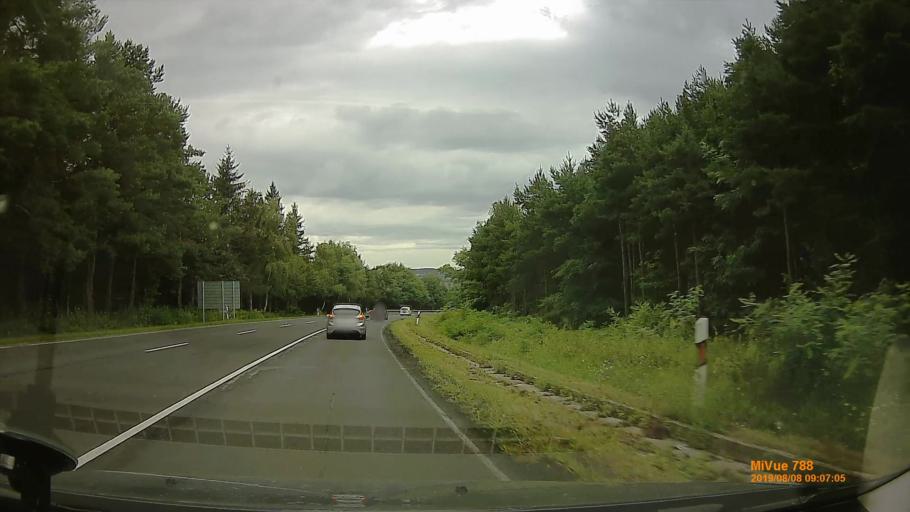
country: HU
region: Zala
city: Zalaegerszeg
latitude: 46.7309
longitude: 16.8568
